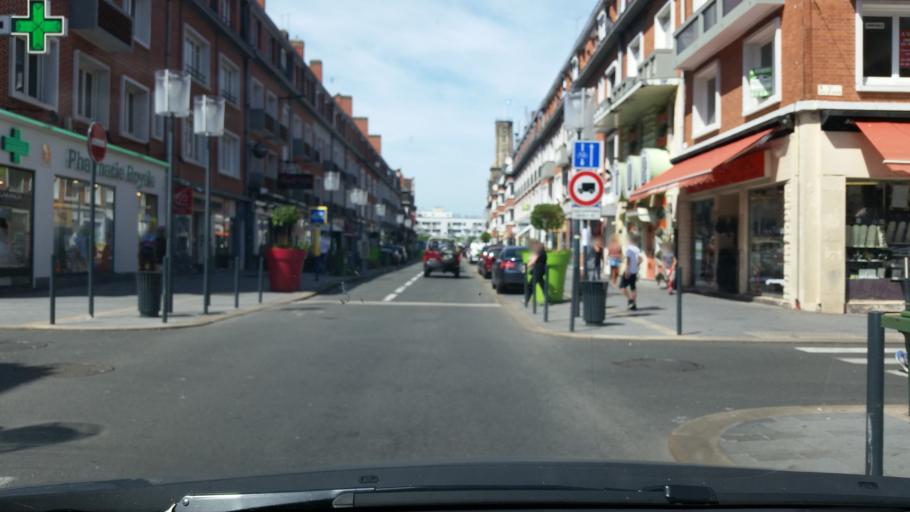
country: FR
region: Nord-Pas-de-Calais
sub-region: Departement du Pas-de-Calais
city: Calais
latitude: 50.9571
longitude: 1.8495
